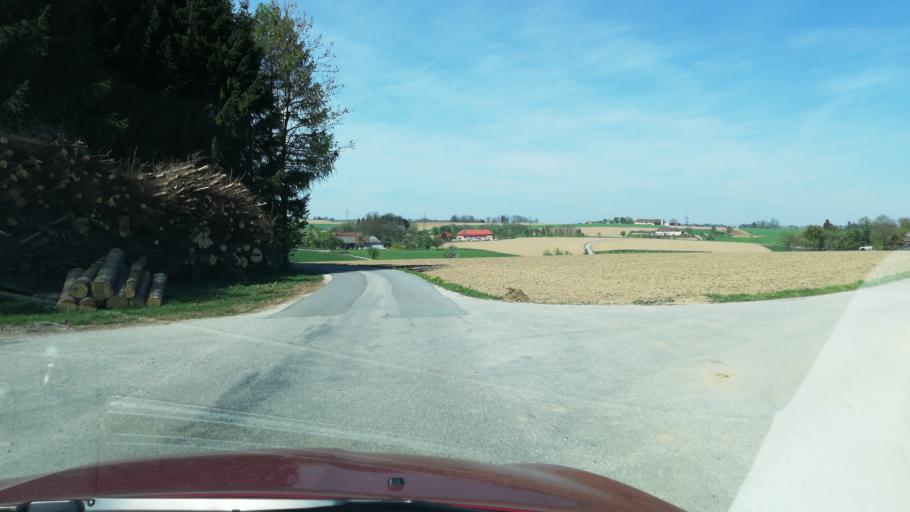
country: AT
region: Upper Austria
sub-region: Politischer Bezirk Steyr-Land
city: Pfarrkirchen bei Bad Hall
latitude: 48.0370
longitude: 14.1811
